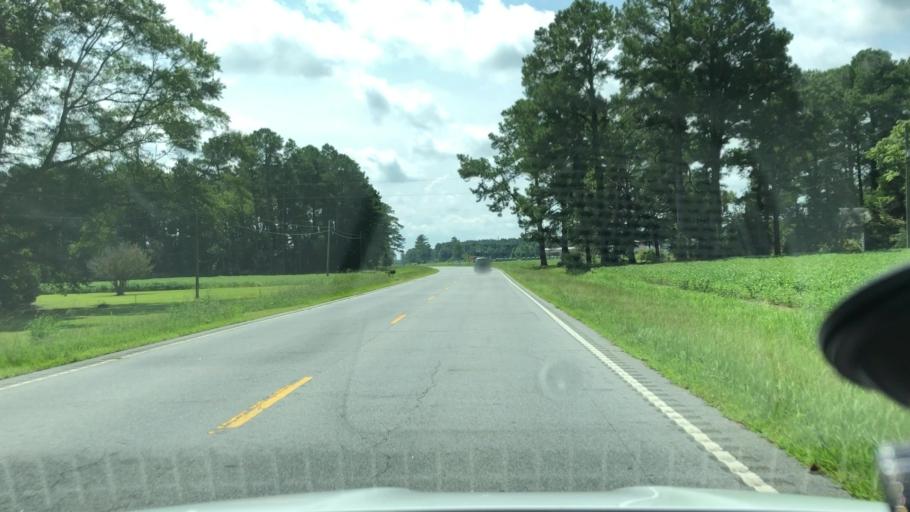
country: US
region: North Carolina
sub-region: Beaufort County
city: Washington
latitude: 35.6553
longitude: -77.0717
